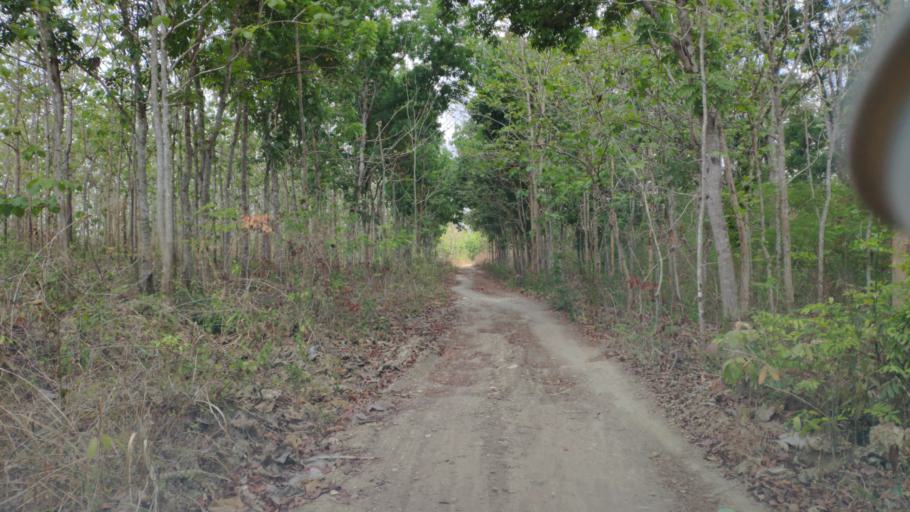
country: ID
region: Central Java
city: Singonegoro
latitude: -6.9908
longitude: 111.5366
